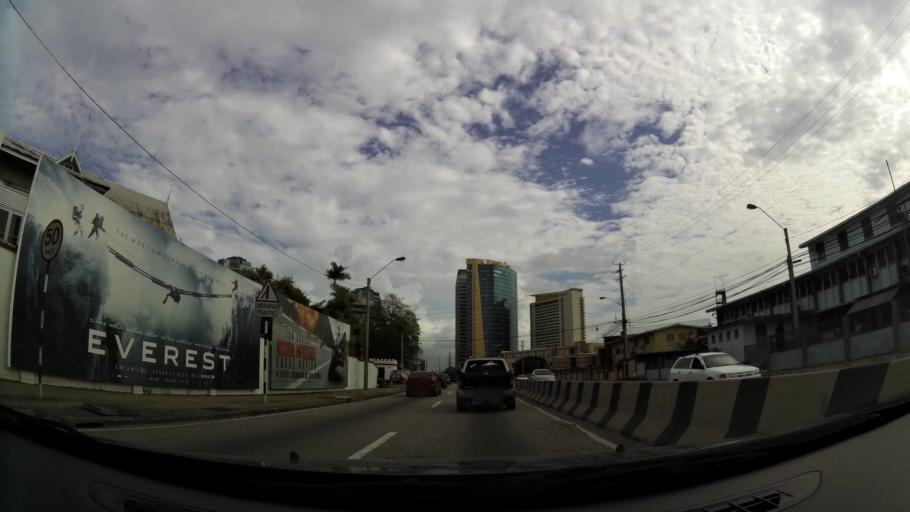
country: TT
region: City of Port of Spain
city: Port-of-Spain
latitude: 10.6542
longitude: -61.5174
